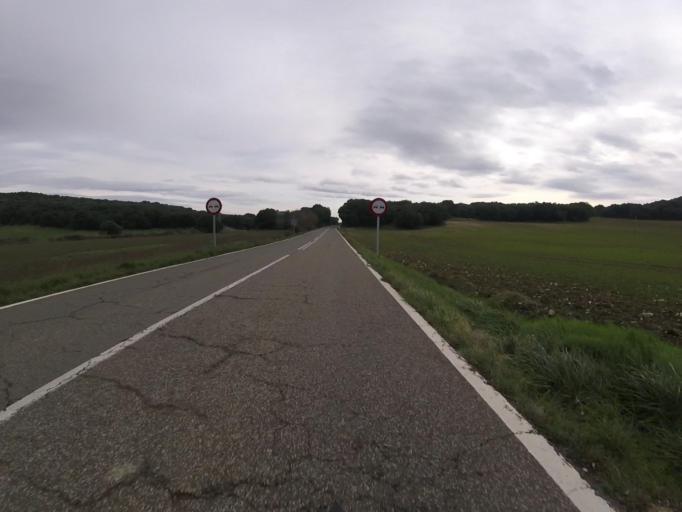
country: ES
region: Navarre
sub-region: Provincia de Navarra
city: Lezaun
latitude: 42.7390
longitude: -2.0184
